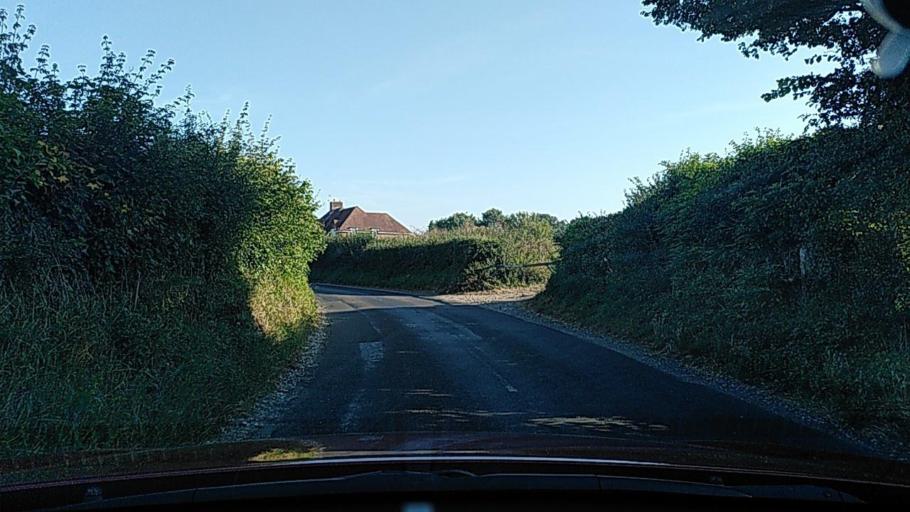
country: GB
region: England
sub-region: Wokingham
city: Sonning
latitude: 51.4862
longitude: -0.9370
